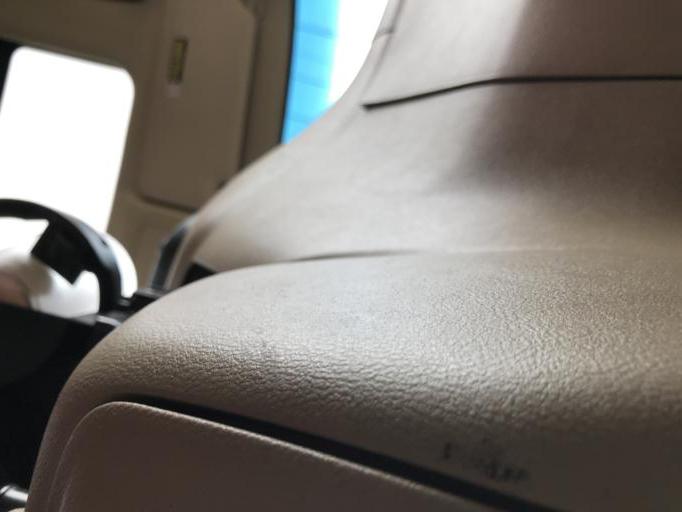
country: US
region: Louisiana
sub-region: Orleans Parish
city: New Orleans
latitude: 29.9327
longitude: -90.0691
